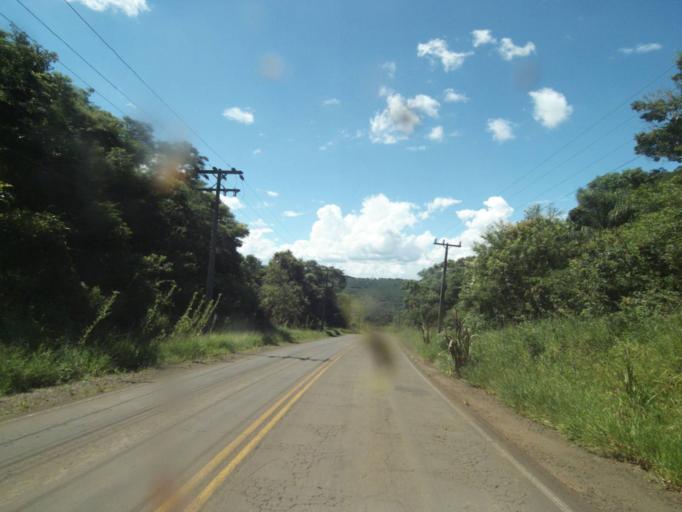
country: BR
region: Parana
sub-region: Chopinzinho
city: Chopinzinho
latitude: -25.7828
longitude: -52.1013
